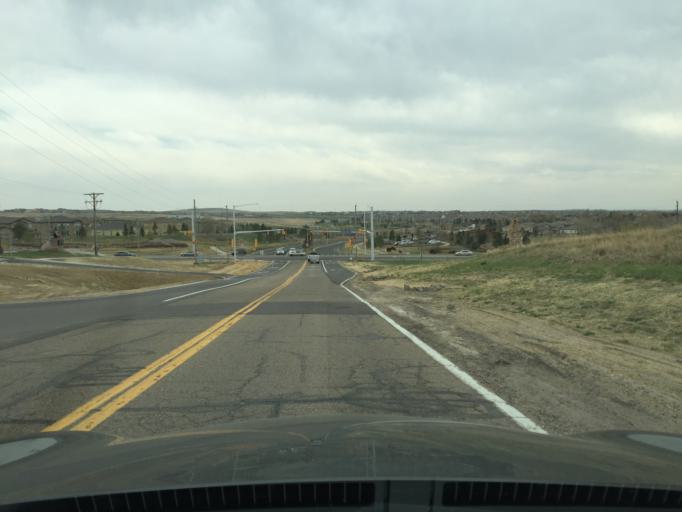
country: US
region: Colorado
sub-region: Boulder County
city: Erie
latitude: 40.0016
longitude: -105.0370
